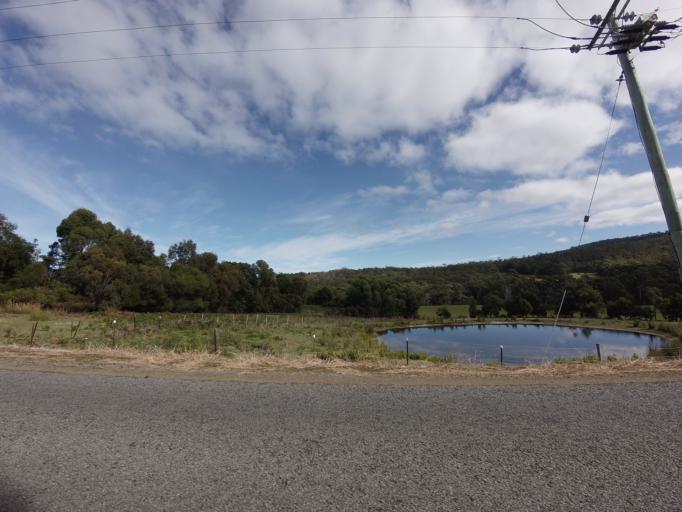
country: AU
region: Tasmania
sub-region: Clarence
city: Sandford
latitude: -43.0874
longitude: 147.7376
